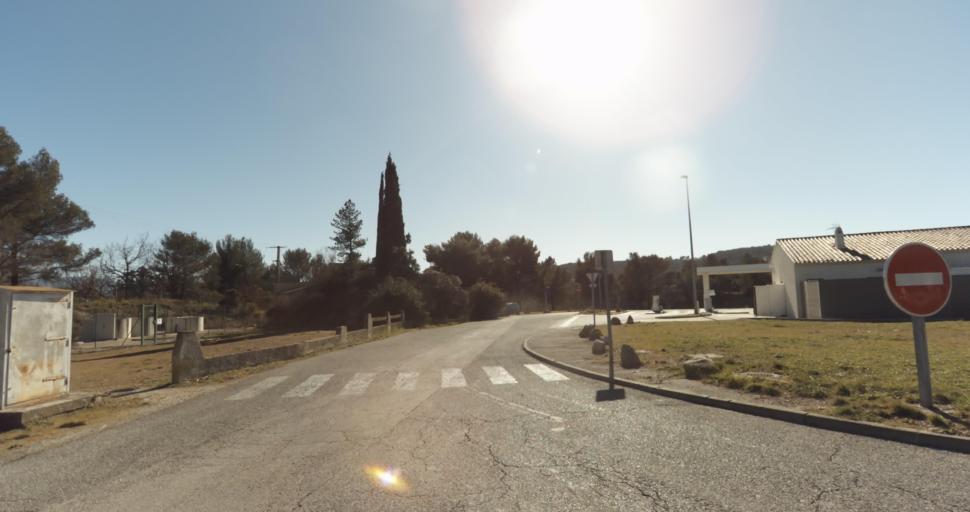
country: FR
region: Provence-Alpes-Cote d'Azur
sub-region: Departement des Bouches-du-Rhone
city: La Bouilladisse
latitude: 43.4009
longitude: 5.5783
